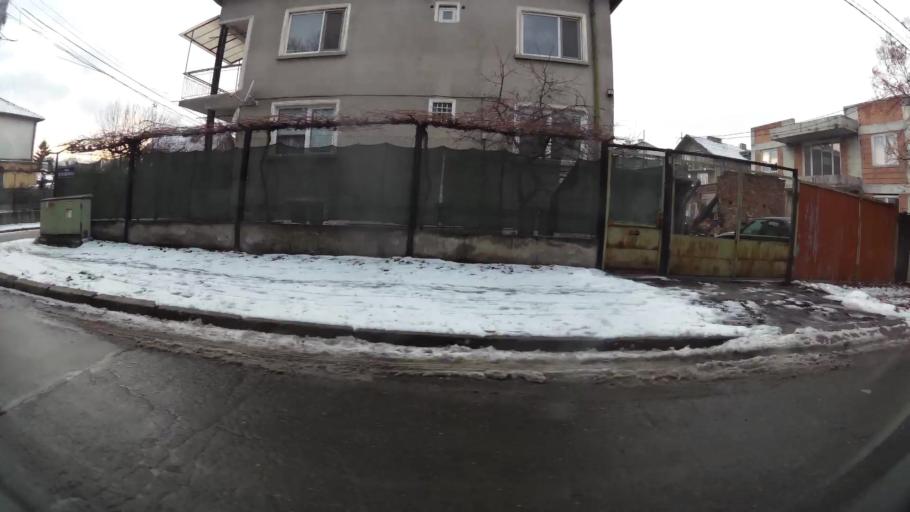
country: BG
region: Sofia-Capital
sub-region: Stolichna Obshtina
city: Sofia
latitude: 42.7235
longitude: 23.3348
